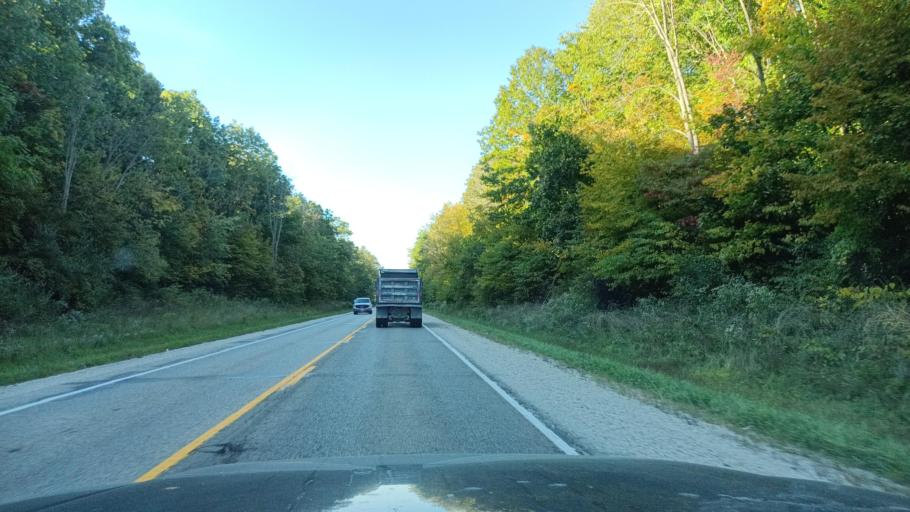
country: US
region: Illinois
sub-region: Clark County
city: Marshall
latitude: 39.4377
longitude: -87.6865
